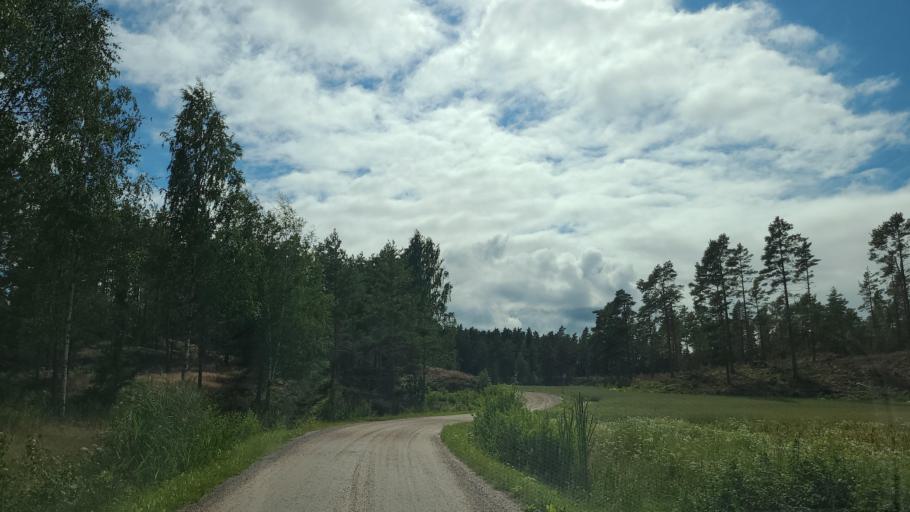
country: FI
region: Varsinais-Suomi
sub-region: Aboland-Turunmaa
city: Nagu
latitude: 60.1886
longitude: 21.7563
